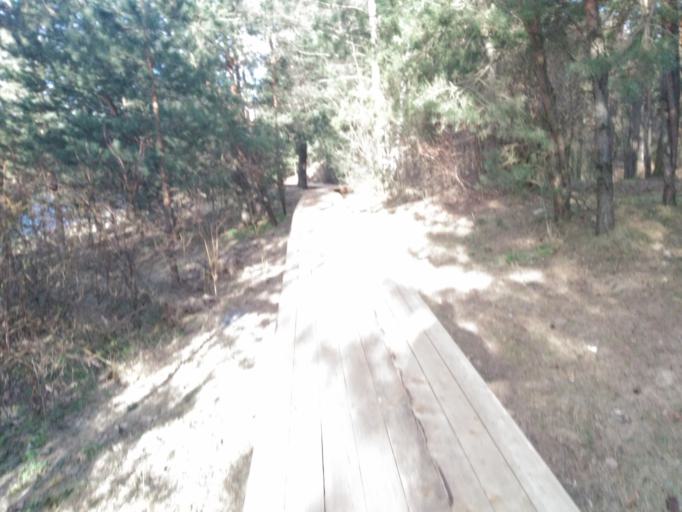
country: RU
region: Moscow
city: Shchukino
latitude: 55.7855
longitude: 37.4306
